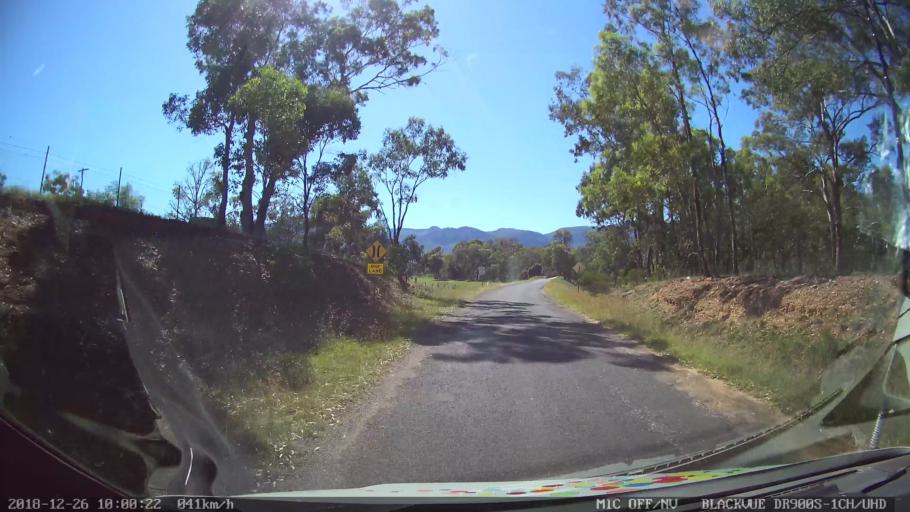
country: AU
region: New South Wales
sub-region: Mid-Western Regional
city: Kandos
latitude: -33.0434
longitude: 150.2157
